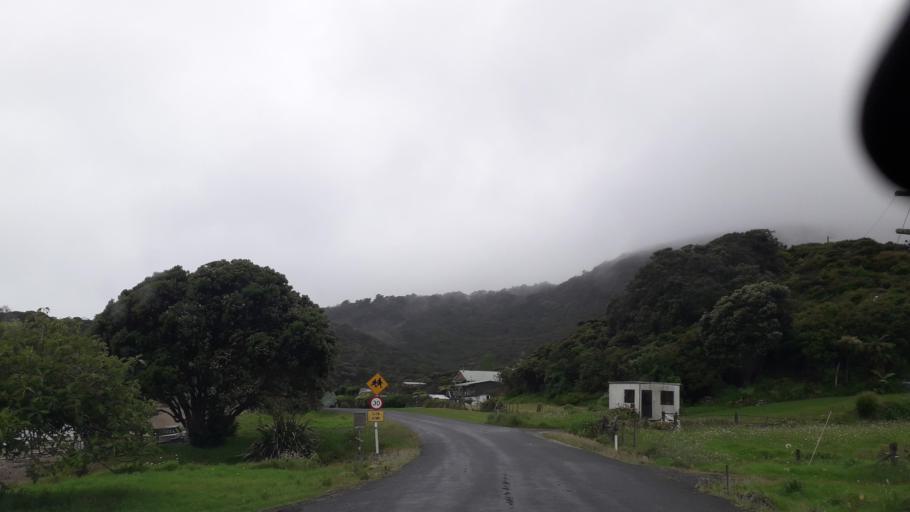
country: NZ
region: Northland
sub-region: Far North District
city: Paihia
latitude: -35.2376
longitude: 174.2582
